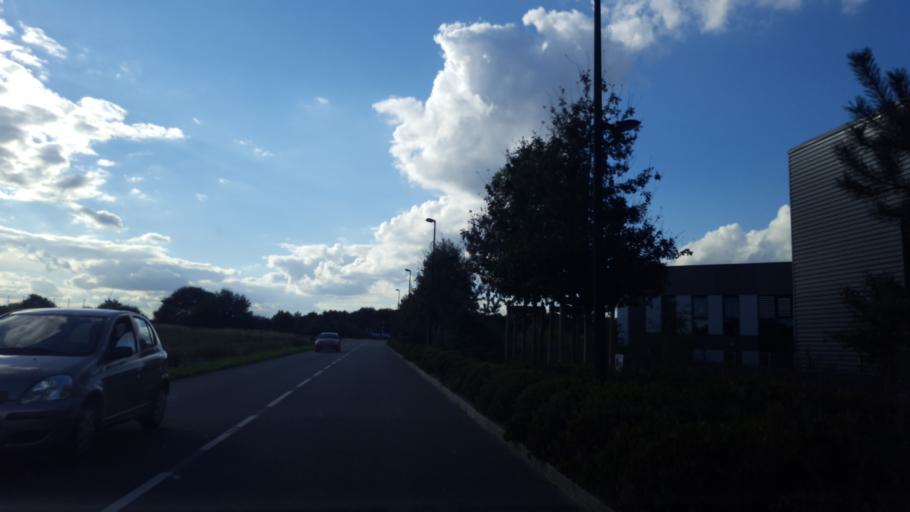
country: FR
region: Brittany
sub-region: Departement d'Ille-et-Vilaine
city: Saint-Jacques-de-la-Lande
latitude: 48.0697
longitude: -1.7084
